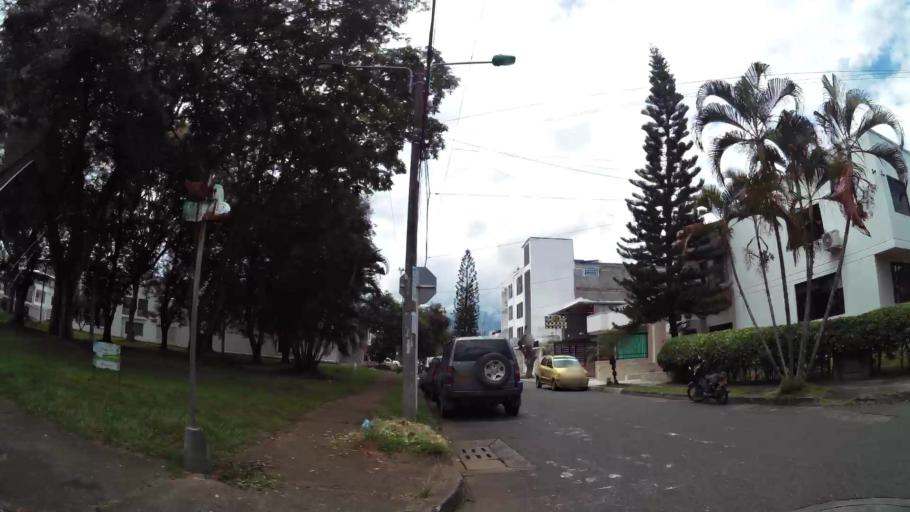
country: CO
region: Valle del Cauca
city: Cali
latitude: 3.3823
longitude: -76.5277
